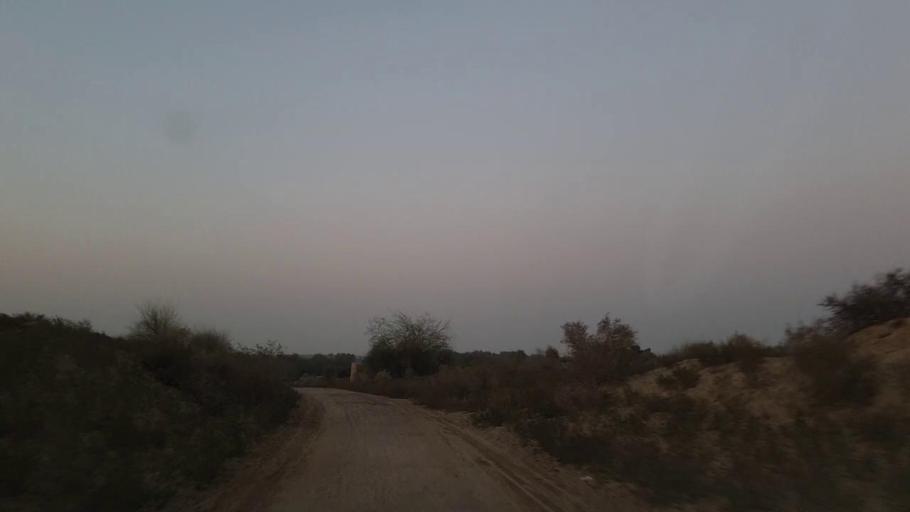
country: PK
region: Sindh
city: Bandhi
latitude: 26.6249
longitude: 68.3953
